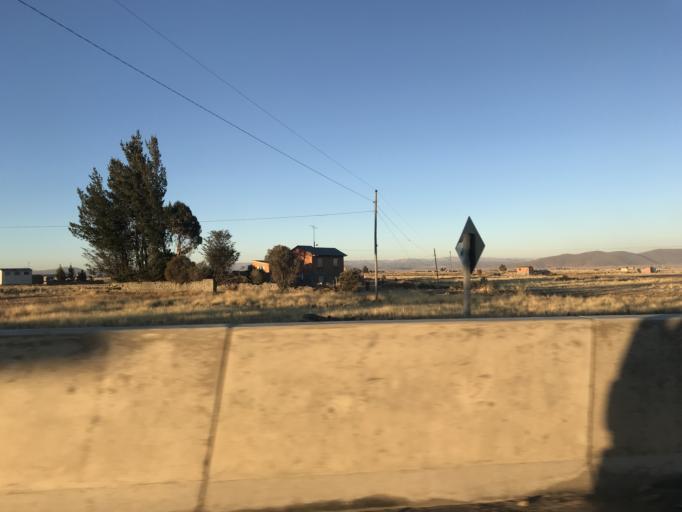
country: BO
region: La Paz
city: Batallas
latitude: -16.3079
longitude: -68.4682
